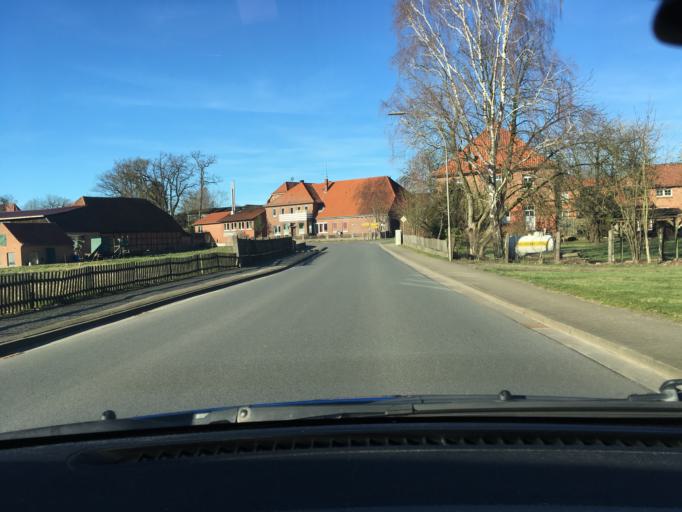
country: DE
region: Lower Saxony
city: Hanstedt Eins
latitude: 53.0449
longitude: 10.3761
